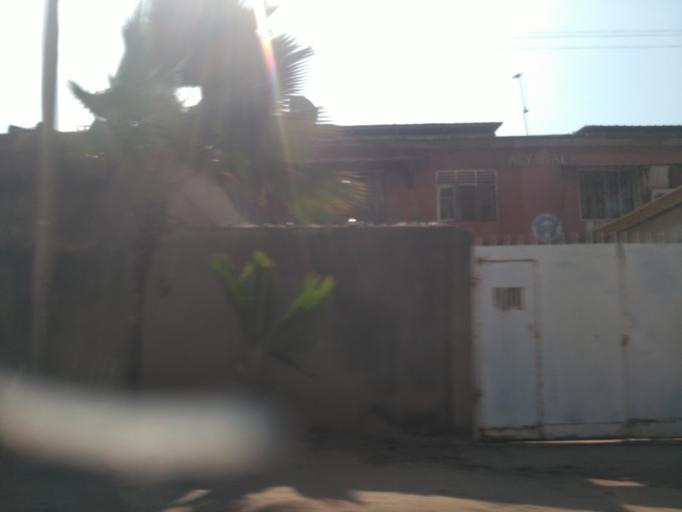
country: TZ
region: Dar es Salaam
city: Dar es Salaam
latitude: -6.8031
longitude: 39.2849
